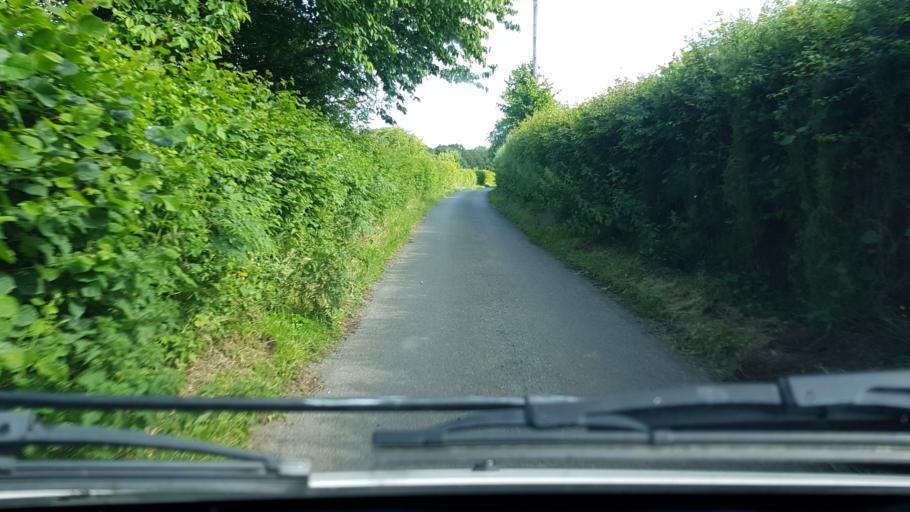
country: GB
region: England
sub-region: Worcestershire
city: Bewdley
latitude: 52.3575
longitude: -2.3281
